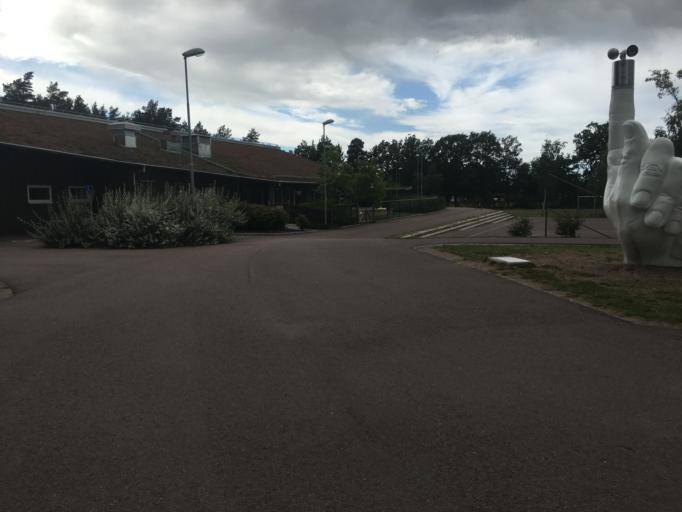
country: SE
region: Kalmar
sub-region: Kalmar Kommun
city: Kalmar
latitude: 56.7014
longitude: 16.3565
